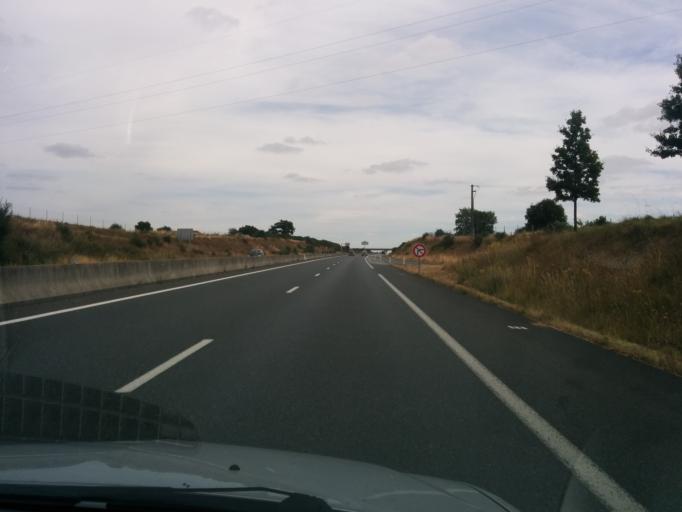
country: FR
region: Poitou-Charentes
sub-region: Departement des Deux-Sevres
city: Saint-Pierre-des-Echaubrognes
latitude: 46.9294
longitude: -0.7259
